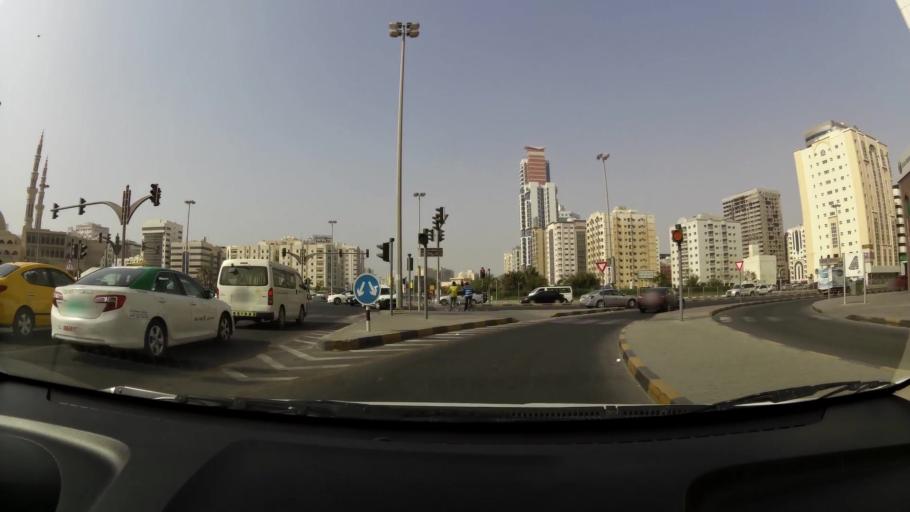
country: AE
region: Ash Shariqah
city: Sharjah
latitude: 25.3476
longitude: 55.3882
